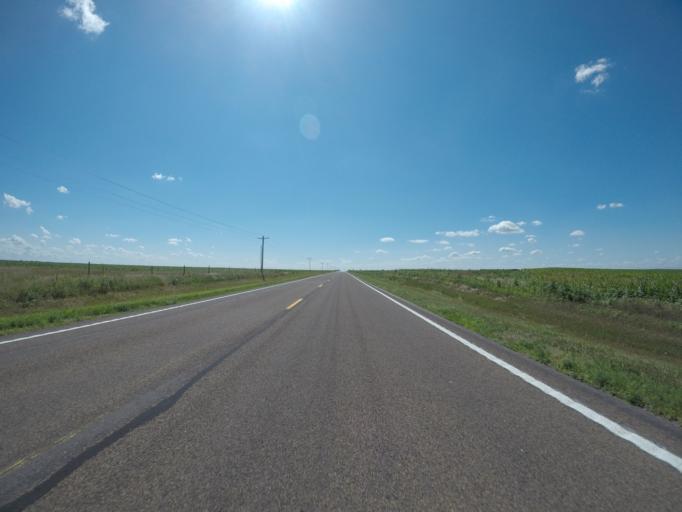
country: US
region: Nebraska
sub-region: Chase County
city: Imperial
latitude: 40.5377
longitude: -101.6914
